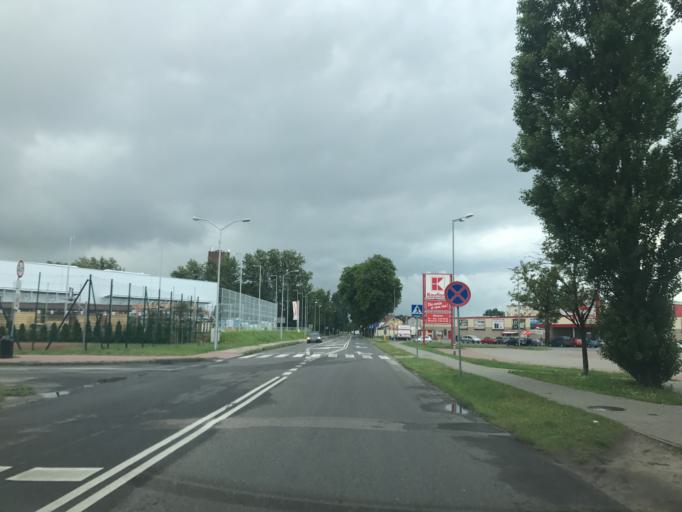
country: PL
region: West Pomeranian Voivodeship
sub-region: Powiat goleniowski
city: Goleniow
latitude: 53.5716
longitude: 14.8312
